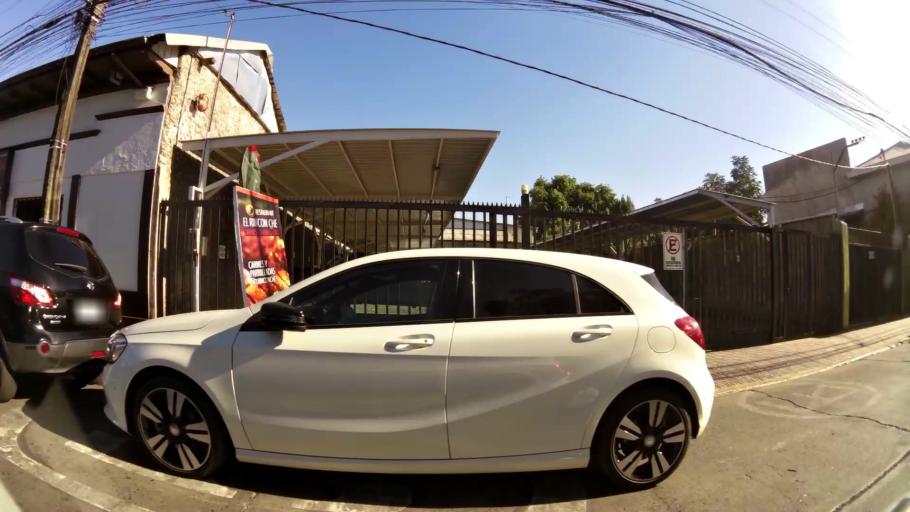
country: CL
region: Maule
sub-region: Provincia de Curico
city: Curico
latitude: -34.9868
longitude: -71.2378
